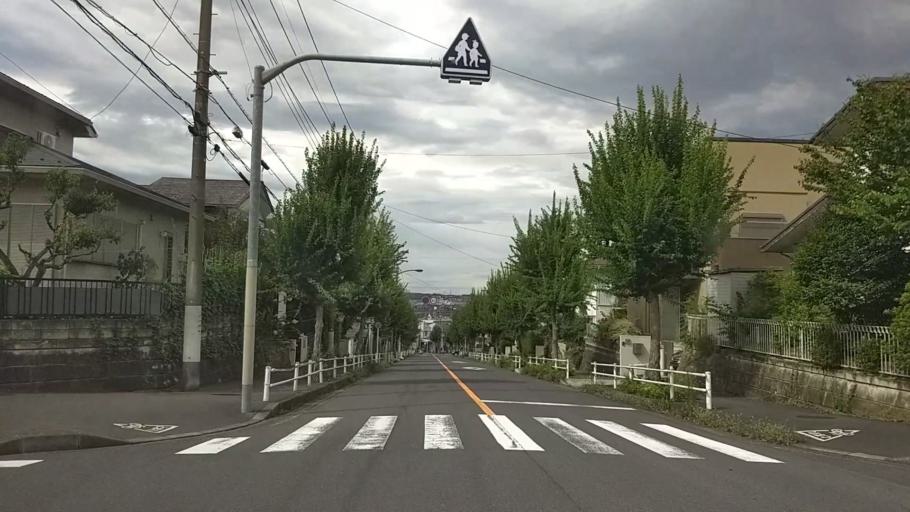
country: JP
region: Tokyo
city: Hachioji
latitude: 35.6393
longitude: 139.3457
